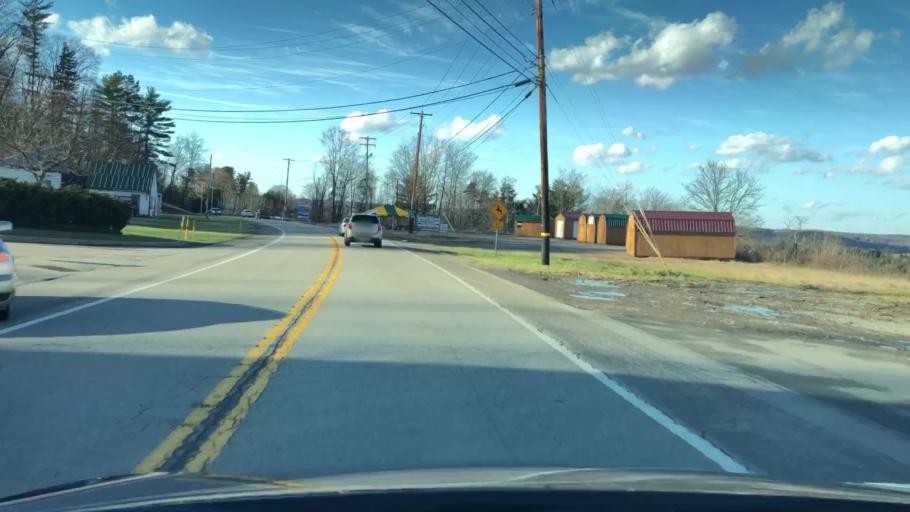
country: US
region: Pennsylvania
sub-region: Armstrong County
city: Freeport
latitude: 40.7079
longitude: -79.7260
